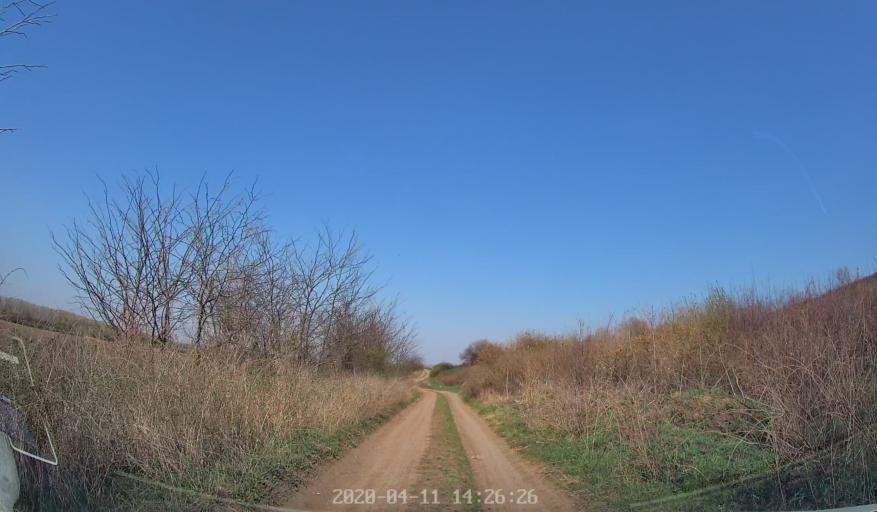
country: MD
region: Chisinau
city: Vadul lui Voda
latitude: 47.0946
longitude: 29.1482
